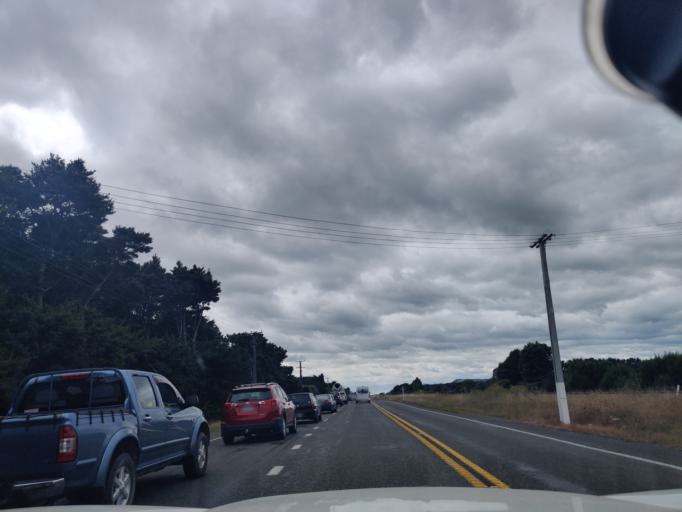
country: NZ
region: Wellington
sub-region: Kapiti Coast District
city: Otaki
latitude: -40.7952
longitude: 175.1269
